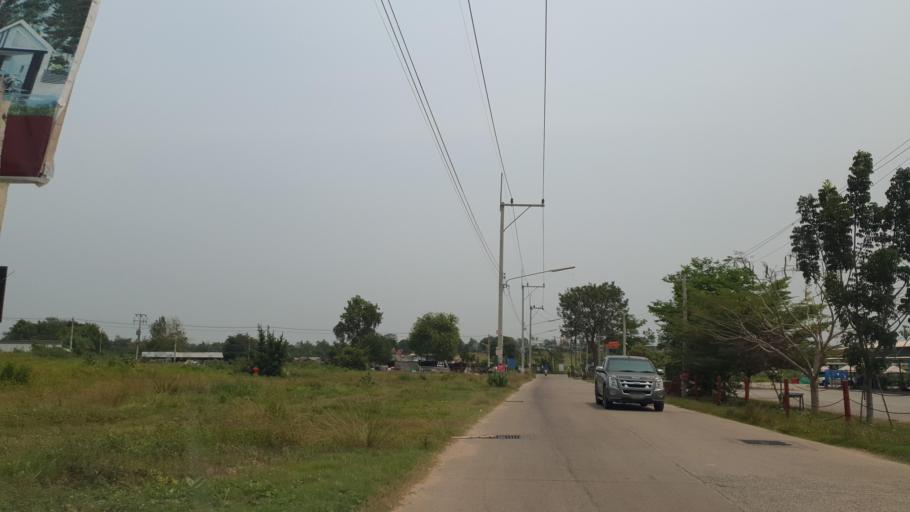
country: TH
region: Chon Buri
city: Phatthaya
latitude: 12.8922
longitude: 100.9275
